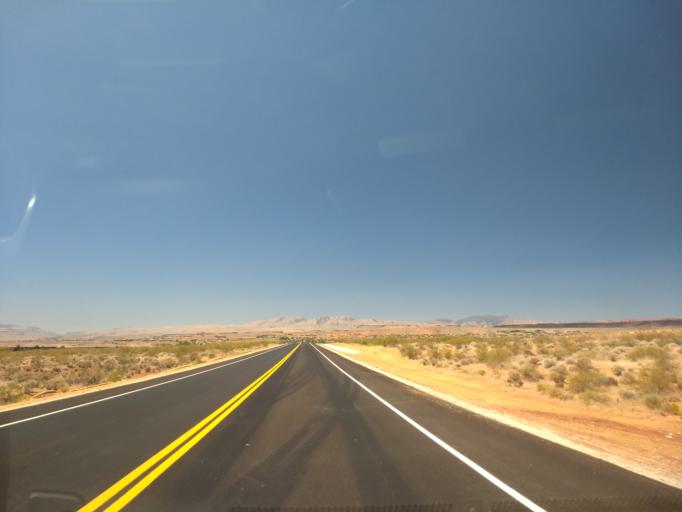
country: US
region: Utah
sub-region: Washington County
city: Washington
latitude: 37.1495
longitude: -113.4984
